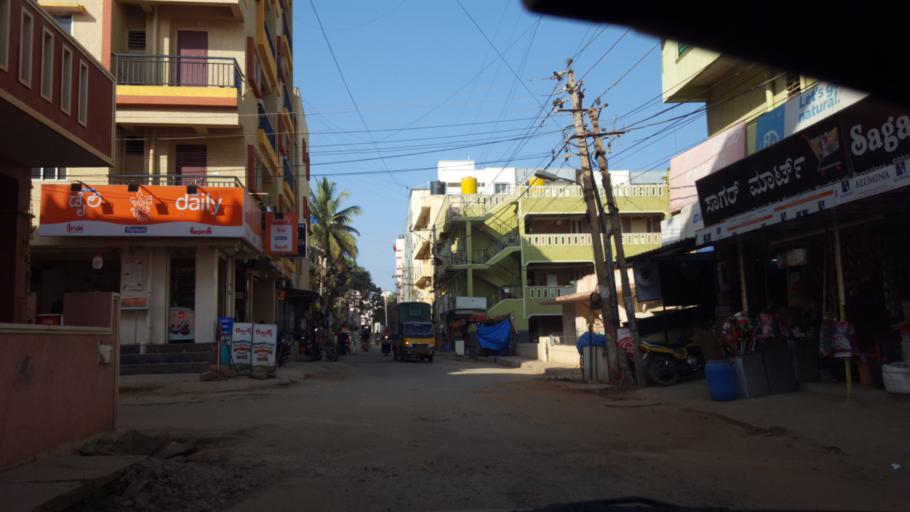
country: IN
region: Karnataka
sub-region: Bangalore Urban
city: Bangalore
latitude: 12.9486
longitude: 77.7091
